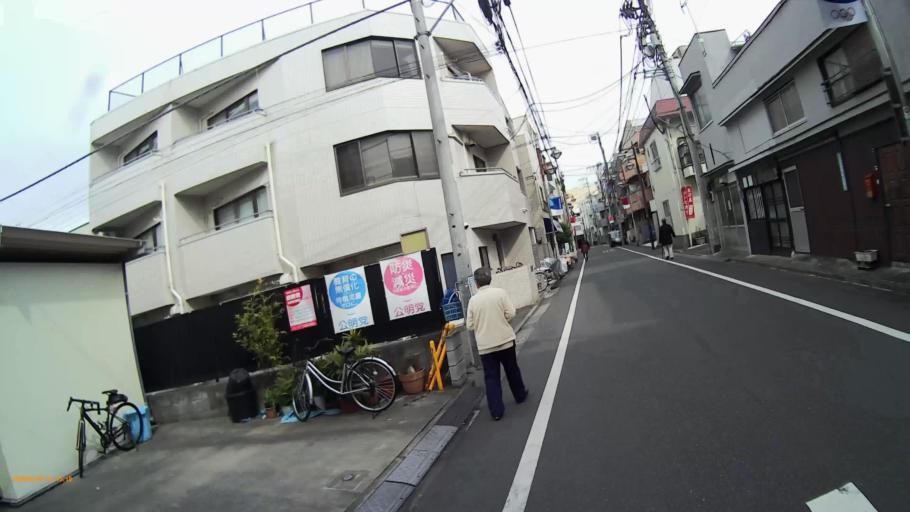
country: JP
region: Tokyo
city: Tokyo
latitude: 35.7419
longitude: 139.7130
